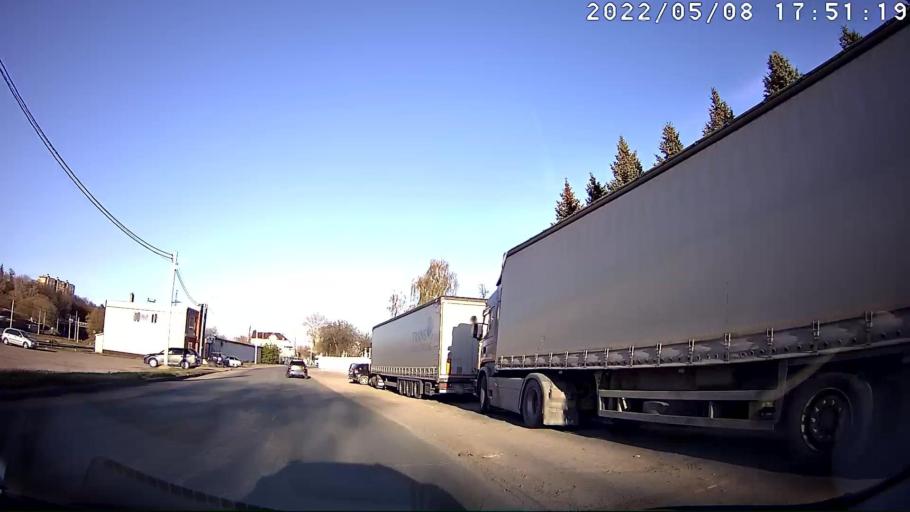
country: RU
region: Tatarstan
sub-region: Zelenodol'skiy Rayon
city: Zelenodolsk
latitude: 55.8413
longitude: 48.4930
